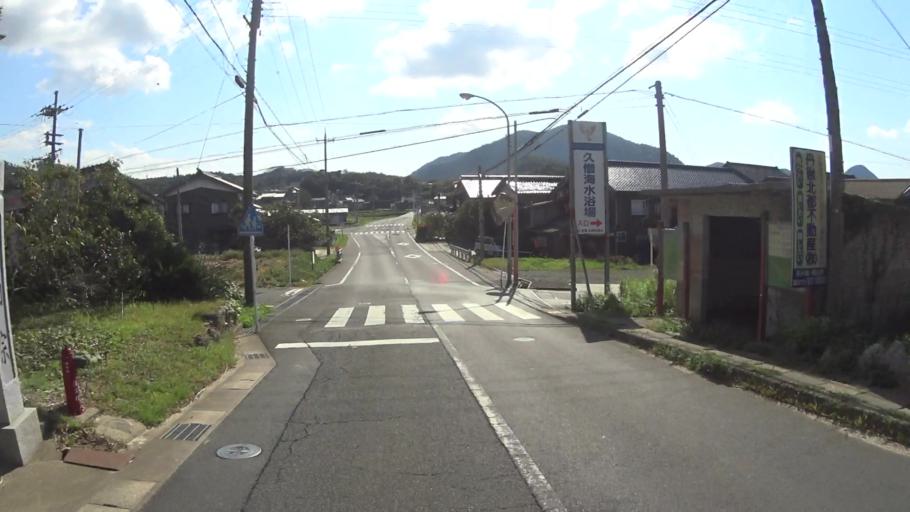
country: JP
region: Kyoto
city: Miyazu
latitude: 35.7567
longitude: 135.1744
